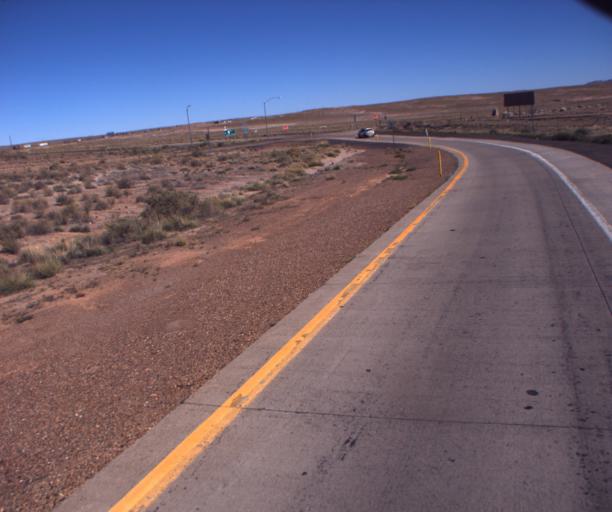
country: US
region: Arizona
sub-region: Navajo County
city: Holbrook
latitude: 34.9719
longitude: -110.0874
